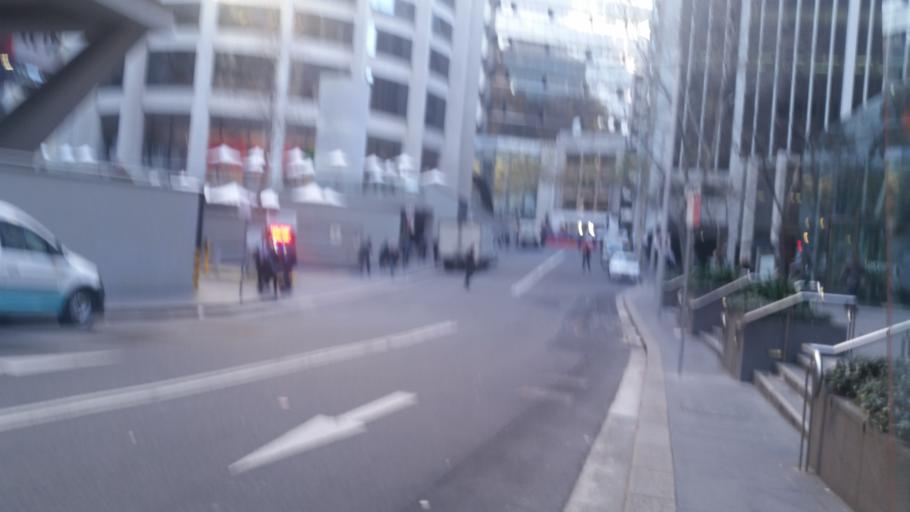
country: AU
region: New South Wales
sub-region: City of Sydney
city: Sydney
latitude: -33.8645
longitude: 151.2088
